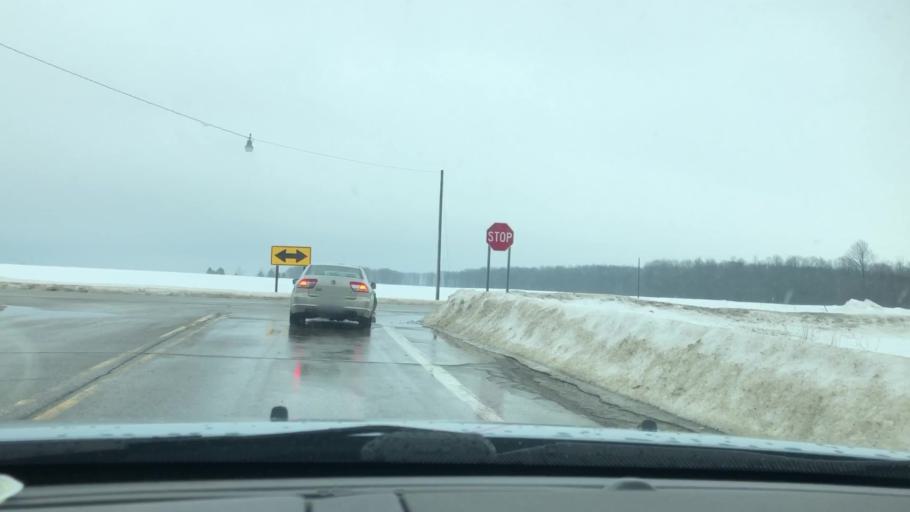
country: US
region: Michigan
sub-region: Charlevoix County
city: Boyne City
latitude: 45.0740
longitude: -84.9002
